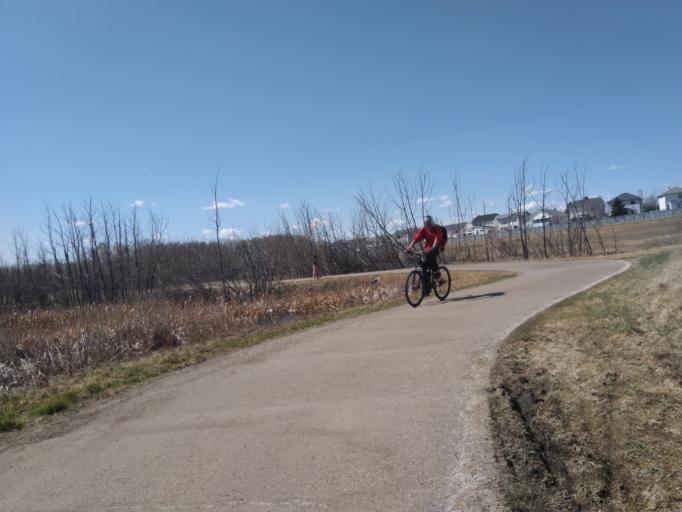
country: CA
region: Alberta
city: Chestermere
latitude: 51.0841
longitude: -113.9245
